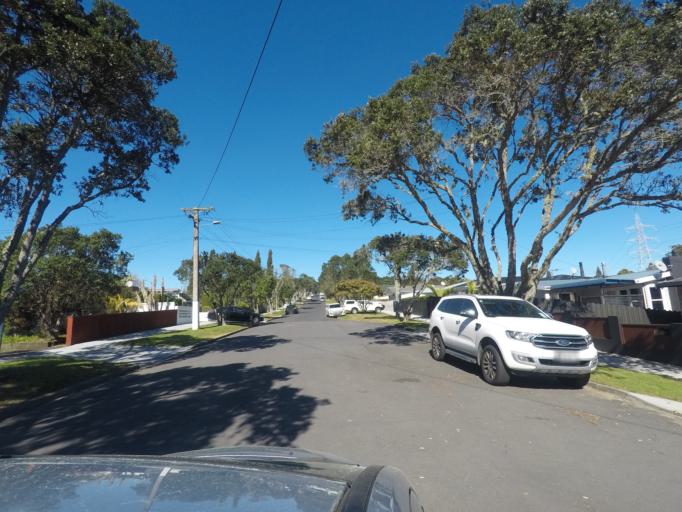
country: NZ
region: Auckland
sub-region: Auckland
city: Waitakere
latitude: -36.9225
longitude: 174.6929
